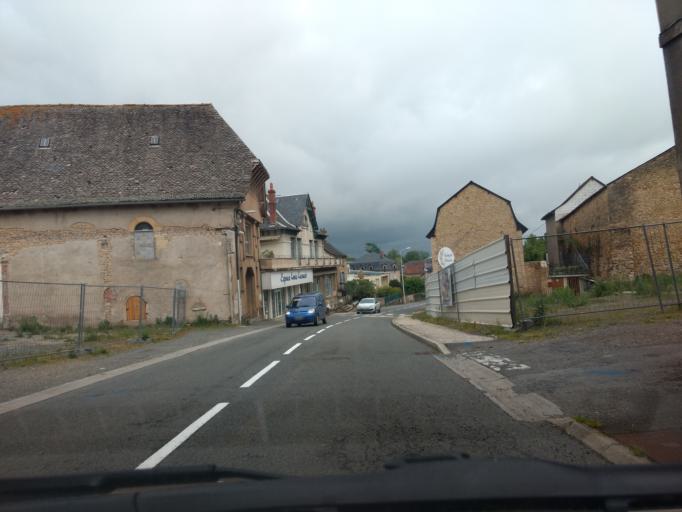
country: FR
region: Midi-Pyrenees
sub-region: Departement de l'Aveyron
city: Montbazens
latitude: 44.4780
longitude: 2.2294
